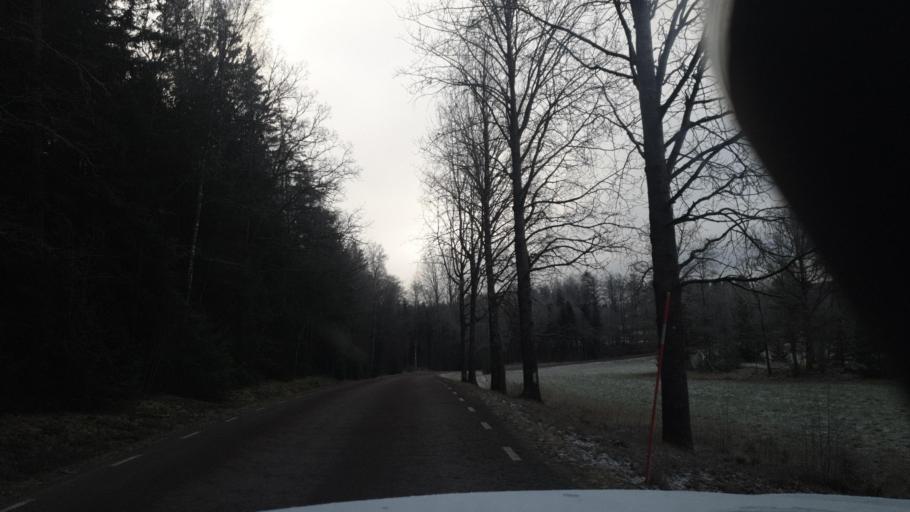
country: SE
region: Vaermland
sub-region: Karlstads Kommun
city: Valberg
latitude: 59.4344
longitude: 13.0876
